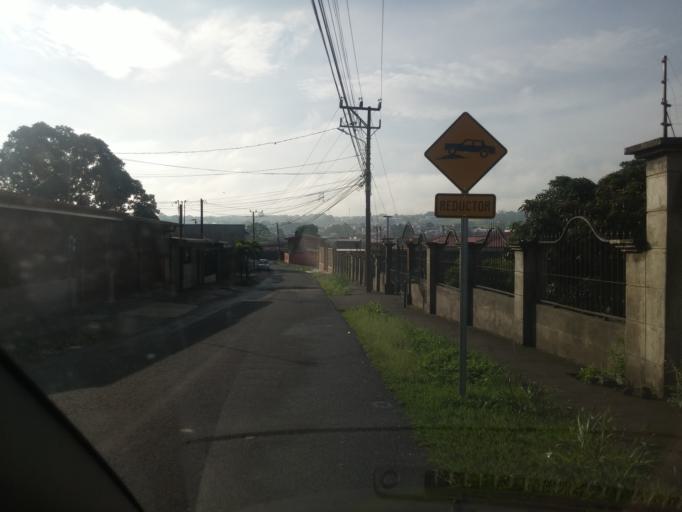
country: CR
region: Heredia
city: Llorente
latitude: 9.9973
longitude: -84.1550
